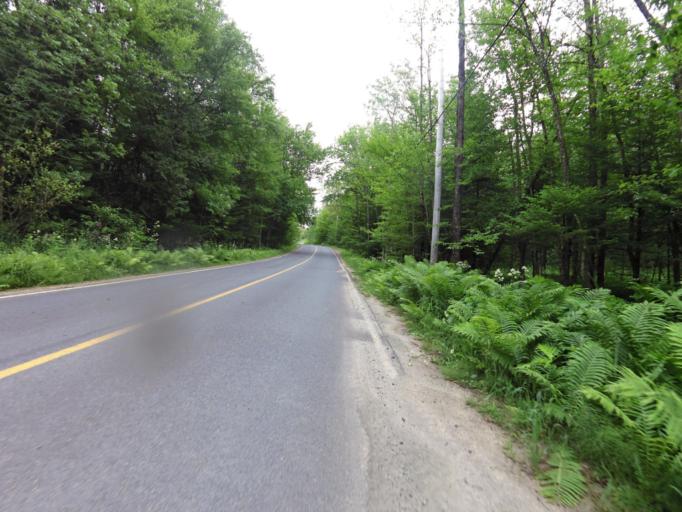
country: CA
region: Quebec
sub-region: Laurentides
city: Brownsburg-Chatham
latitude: 45.8926
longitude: -74.5954
